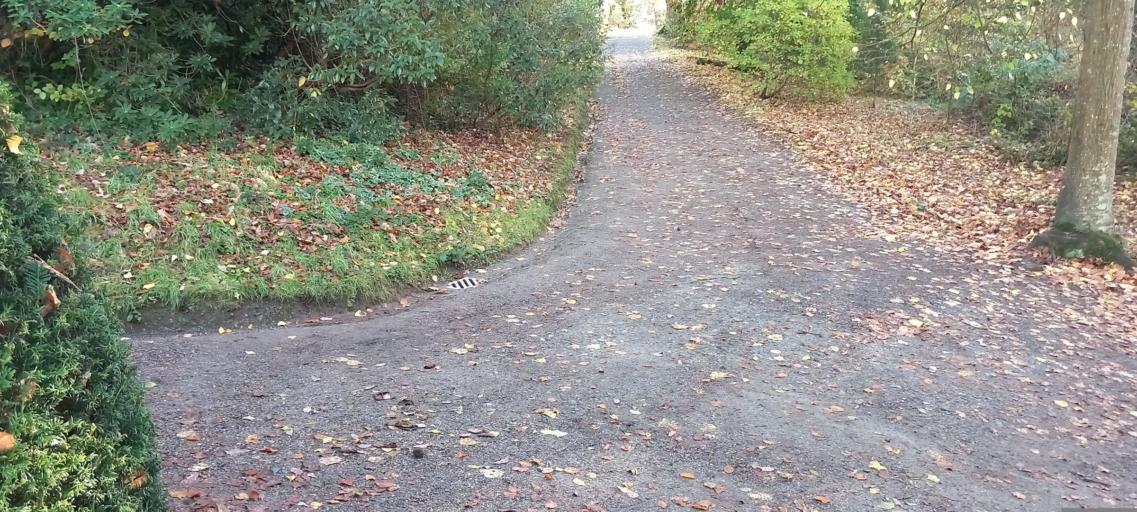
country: GB
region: Wales
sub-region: Gwynedd
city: Bangor
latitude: 53.2258
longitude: -4.0976
